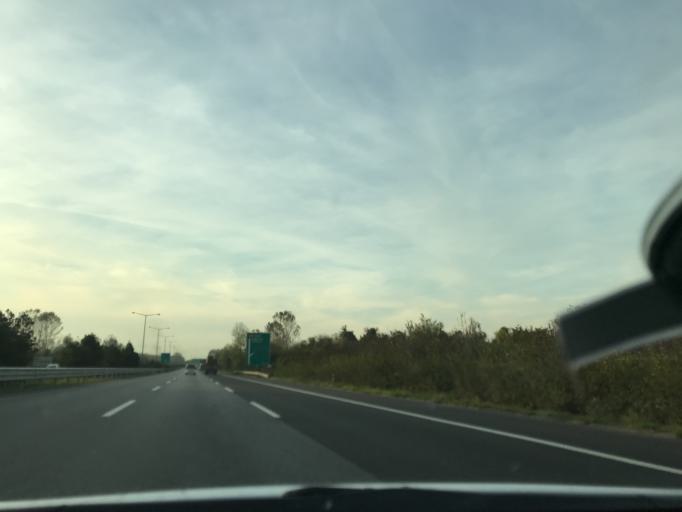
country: TR
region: Duzce
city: Cilimli
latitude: 40.8273
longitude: 31.0522
